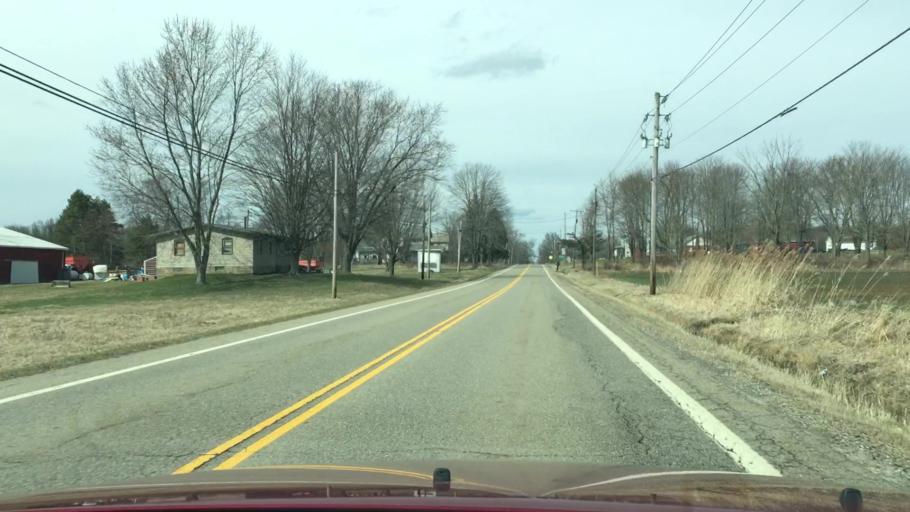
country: US
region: Ohio
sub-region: Mahoning County
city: Sebring
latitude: 41.0162
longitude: -81.0503
